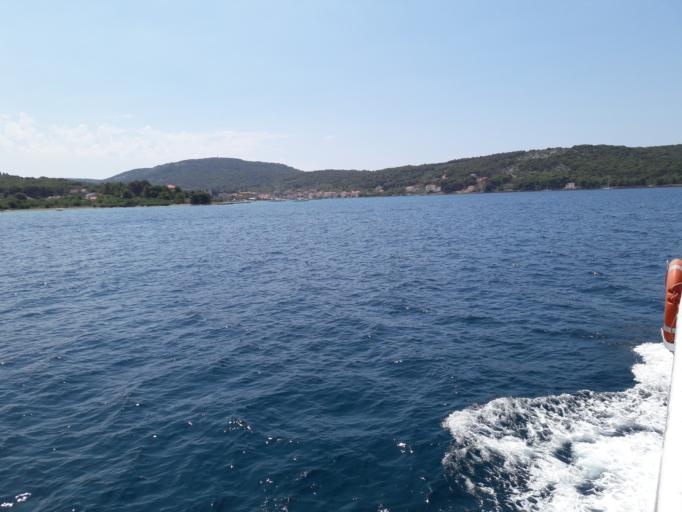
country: HR
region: Sibensko-Kniniska
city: Vodice
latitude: 43.7078
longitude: 15.8315
